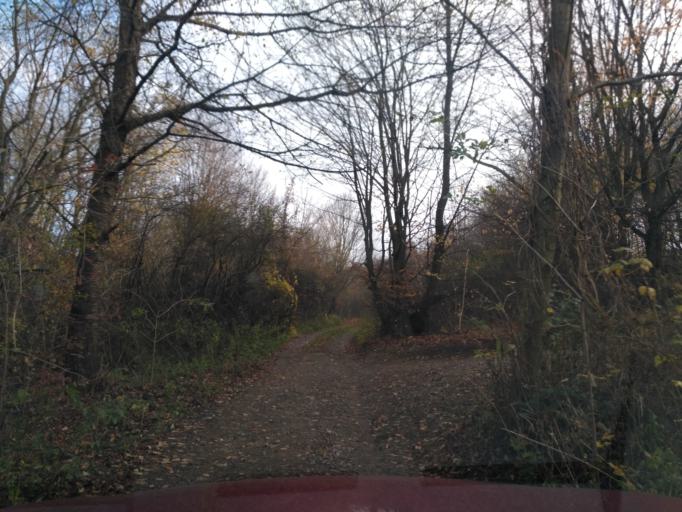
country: SK
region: Presovsky
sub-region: Okres Presov
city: Presov
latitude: 48.8745
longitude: 21.2276
